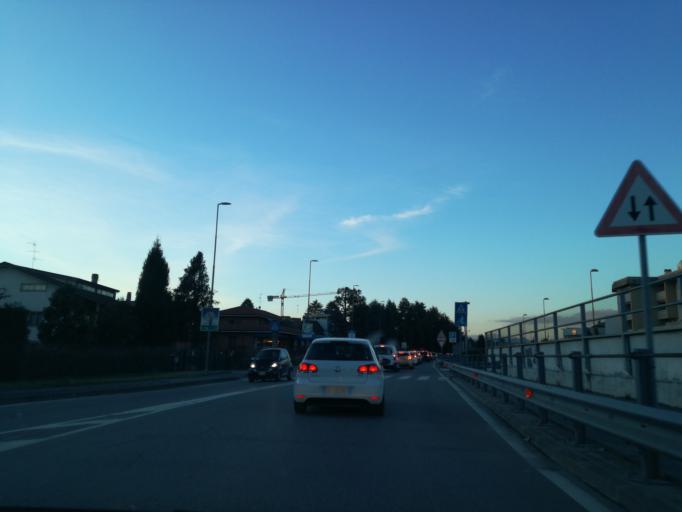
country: IT
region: Lombardy
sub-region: Provincia di Monza e Brianza
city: Vimercate
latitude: 45.6120
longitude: 9.3595
